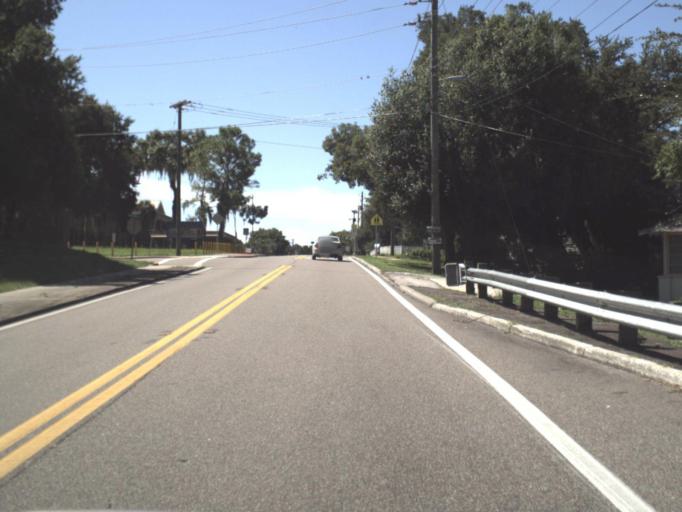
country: US
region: Florida
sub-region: Polk County
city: Auburndale
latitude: 28.0723
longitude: -81.7886
